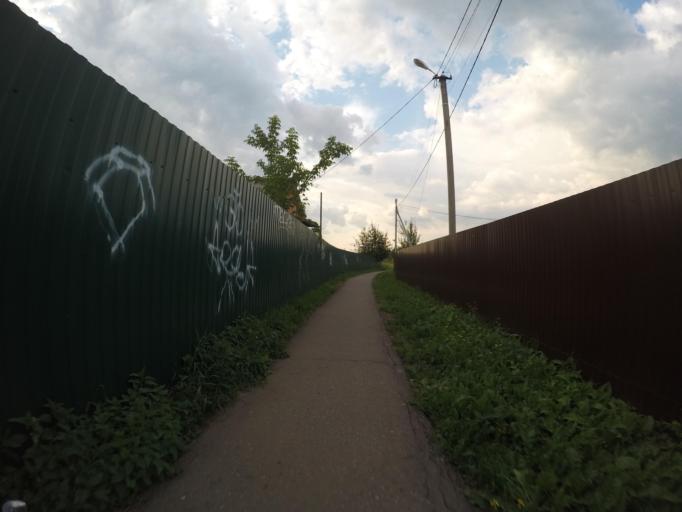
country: RU
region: Moskovskaya
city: Rechitsy
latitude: 55.5983
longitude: 38.5054
